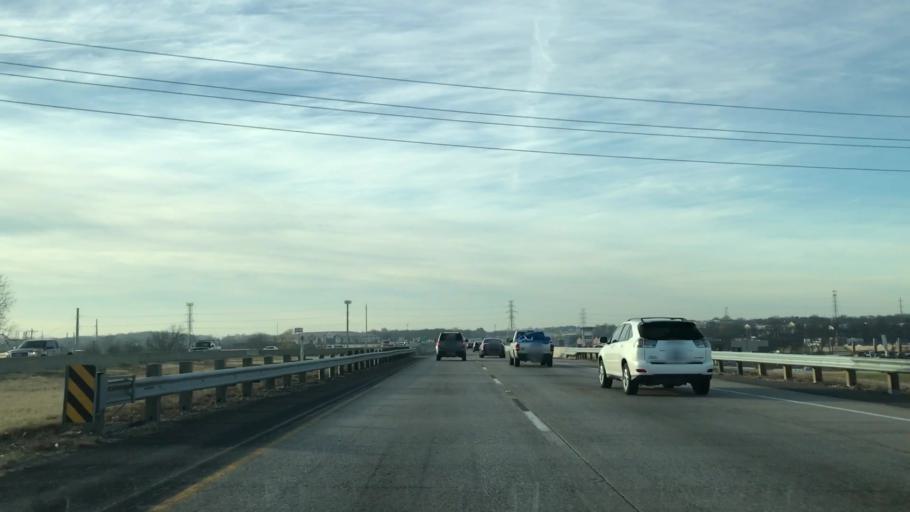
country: US
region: Texas
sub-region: Tarrant County
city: Euless
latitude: 32.8705
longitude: -97.1008
